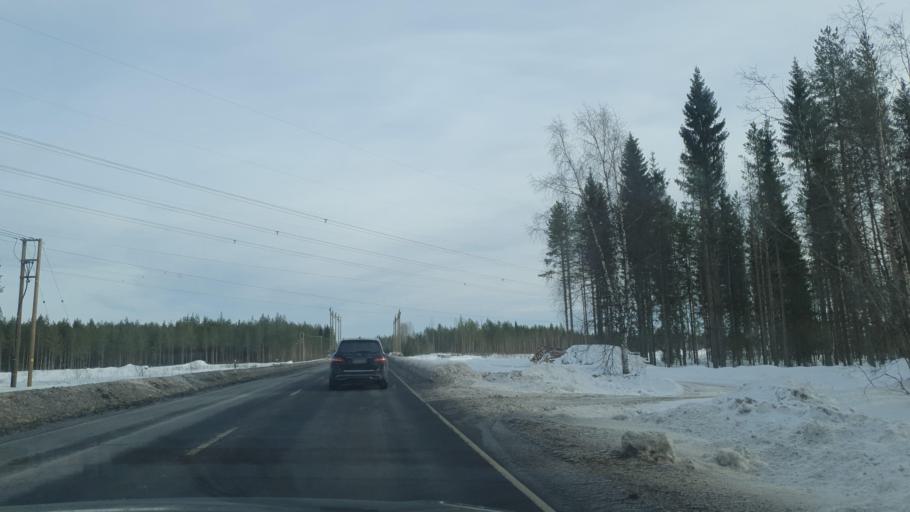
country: FI
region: Northern Ostrobothnia
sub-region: Oulu
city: Muhos
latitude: 64.7863
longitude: 26.1811
